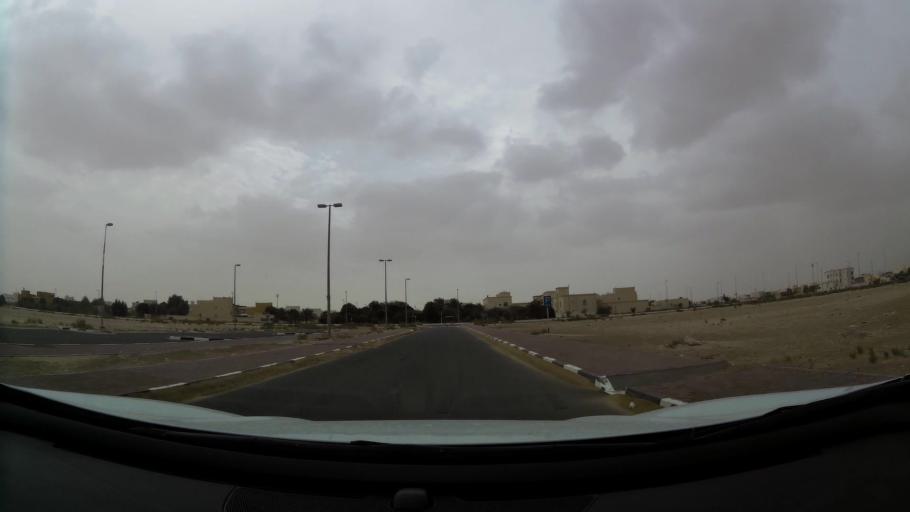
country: AE
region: Abu Dhabi
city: Abu Dhabi
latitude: 24.3720
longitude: 54.6661
